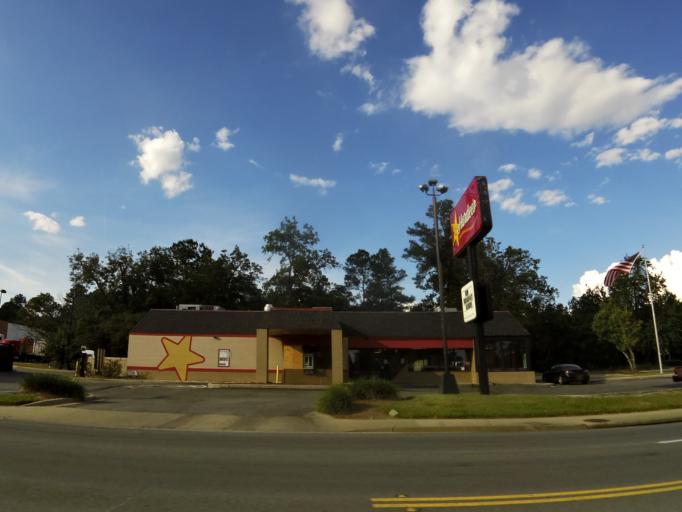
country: US
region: Georgia
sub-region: Brooks County
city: Quitman
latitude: 30.7853
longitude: -83.5704
